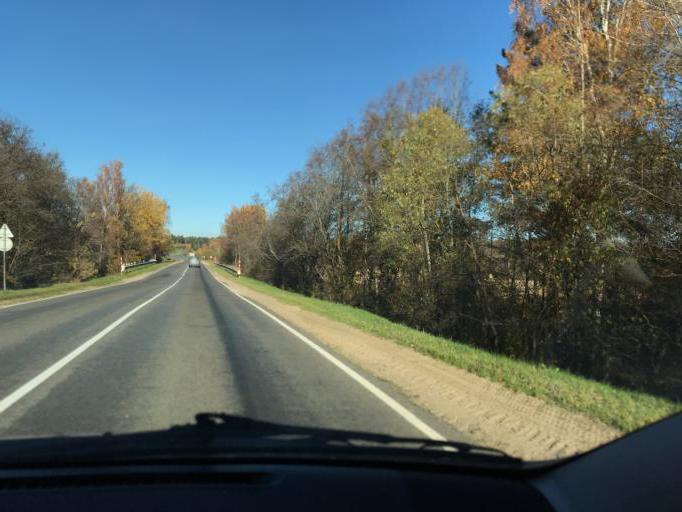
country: BY
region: Vitebsk
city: Polatsk
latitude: 55.3079
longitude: 28.7789
